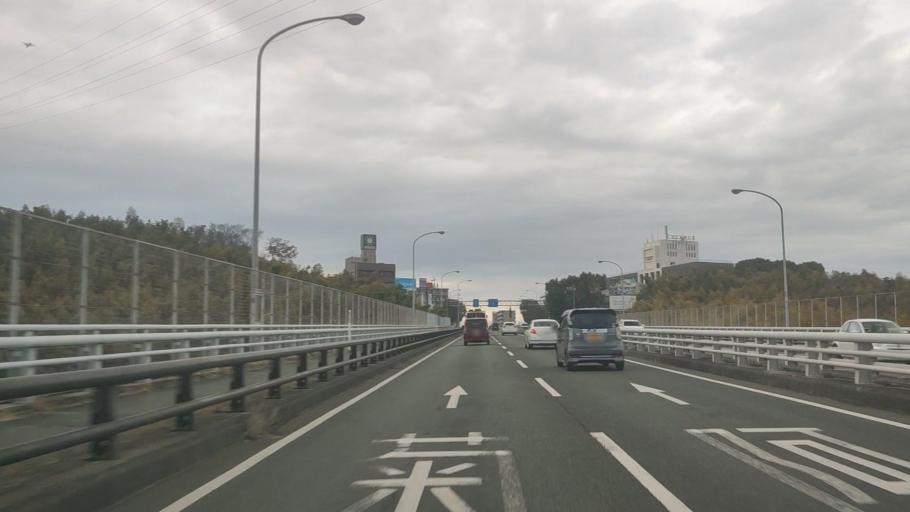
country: JP
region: Kumamoto
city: Ozu
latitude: 32.8490
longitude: 130.7823
